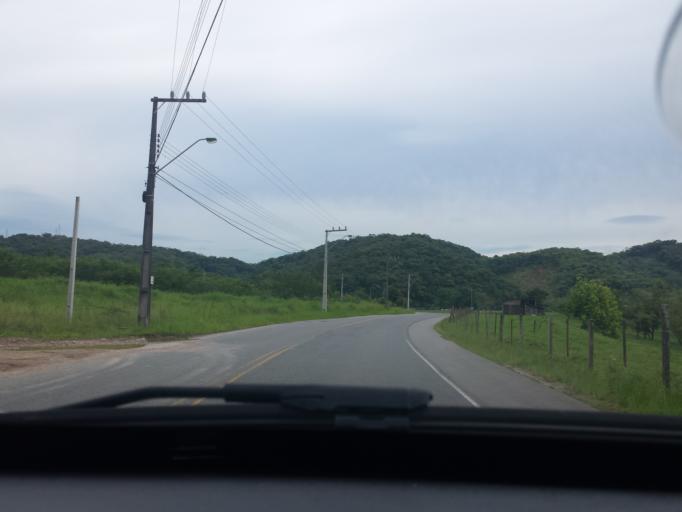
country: BR
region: Santa Catarina
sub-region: Blumenau
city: Blumenau
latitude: -26.9008
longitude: -49.0188
